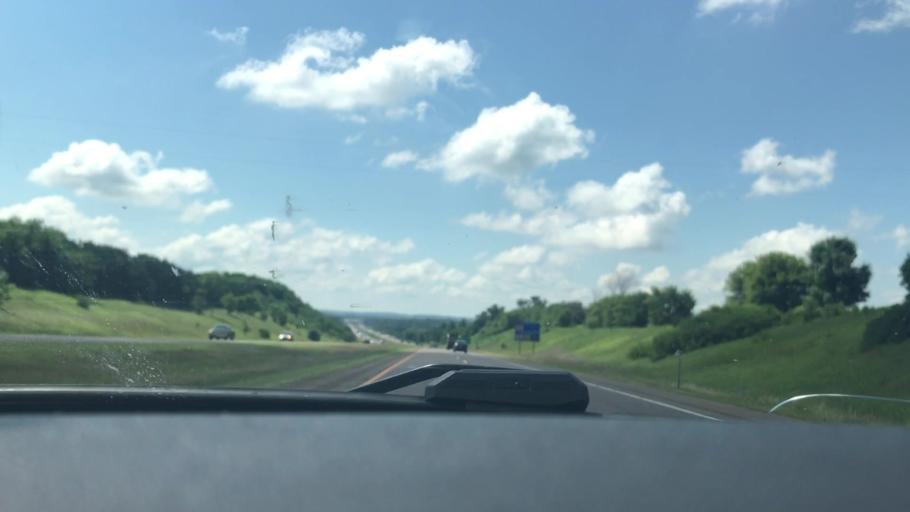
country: US
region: Wisconsin
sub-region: Chippewa County
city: Chippewa Falls
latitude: 44.9373
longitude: -91.4281
